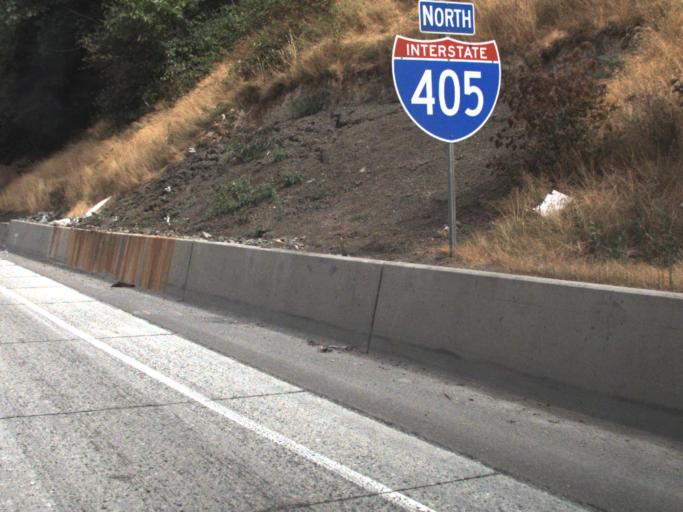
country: US
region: Washington
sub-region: King County
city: Renton
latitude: 47.4749
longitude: -122.2036
